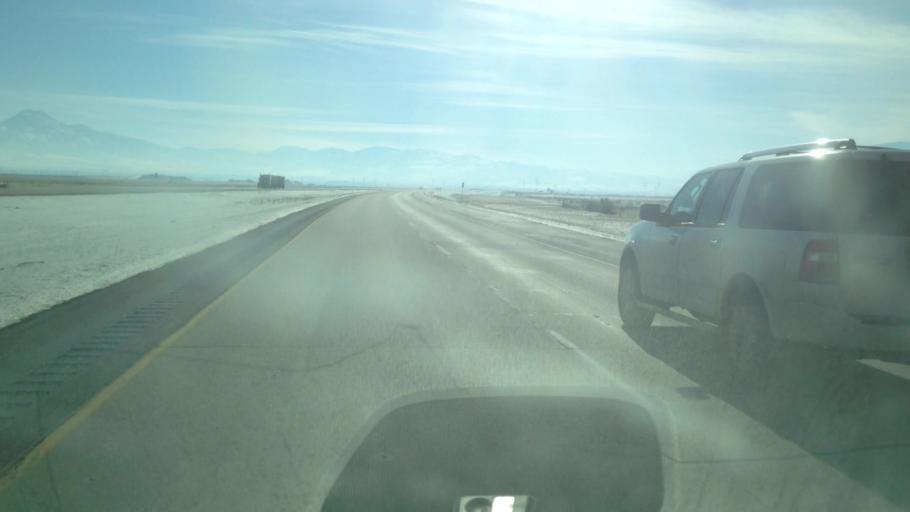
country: US
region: Idaho
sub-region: Oneida County
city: Malad City
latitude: 42.4611
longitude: -112.1697
